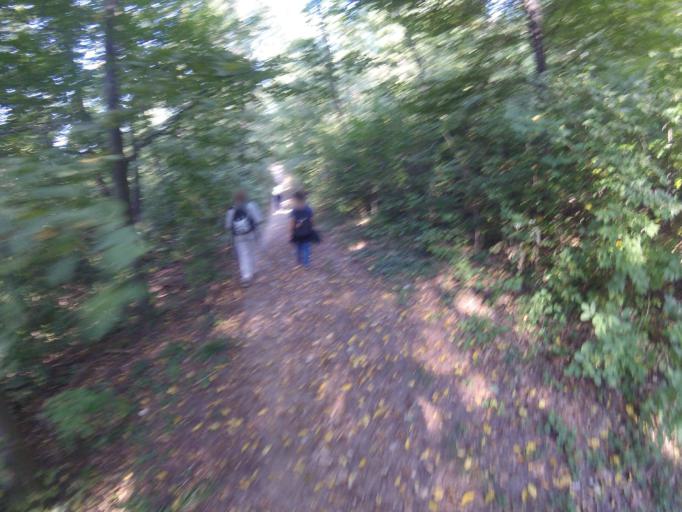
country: HU
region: Komarom-Esztergom
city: Piliscsev
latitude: 47.7038
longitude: 18.8371
